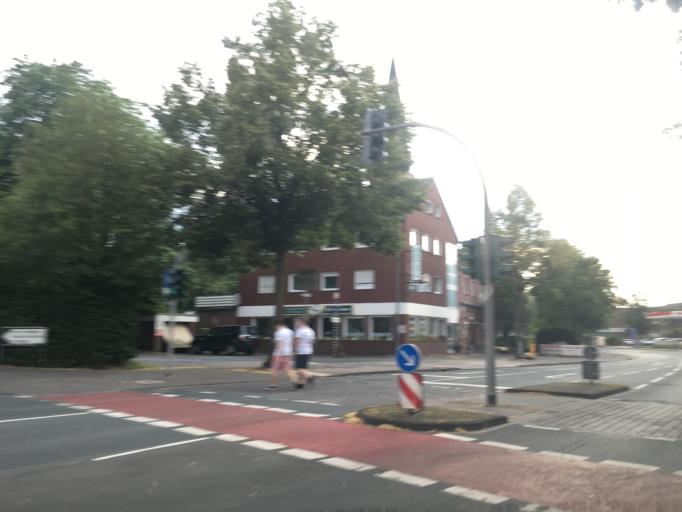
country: DE
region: North Rhine-Westphalia
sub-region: Regierungsbezirk Munster
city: Senden
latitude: 51.9249
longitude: 7.5270
